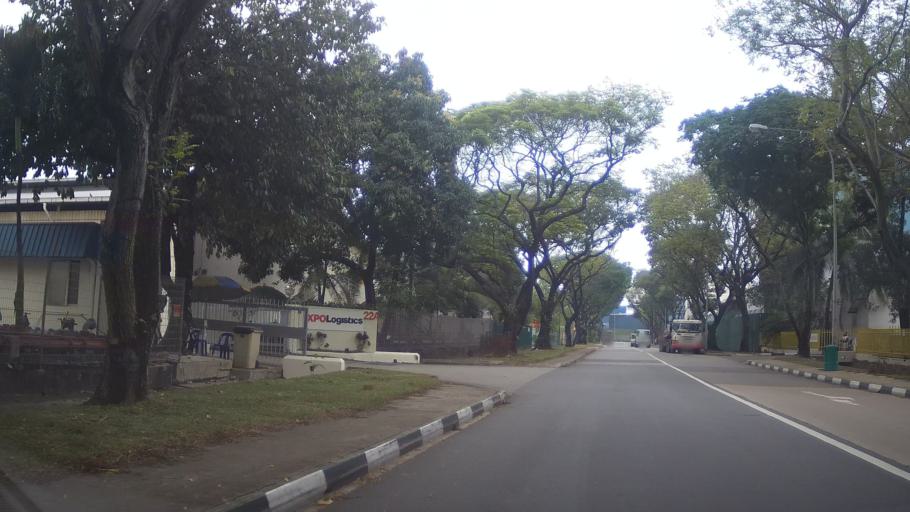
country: SG
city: Singapore
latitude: 1.3052
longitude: 103.6761
